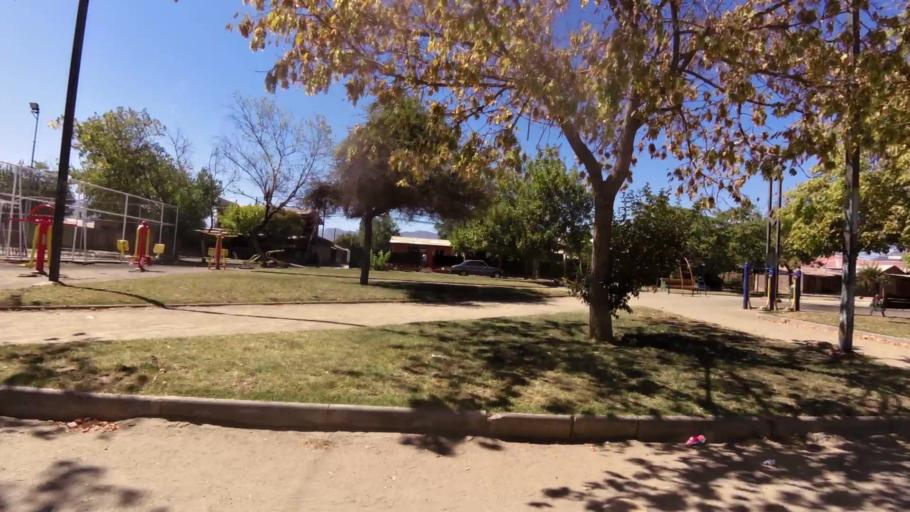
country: CL
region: O'Higgins
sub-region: Provincia de Cachapoal
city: Rancagua
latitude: -34.1660
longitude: -70.7123
